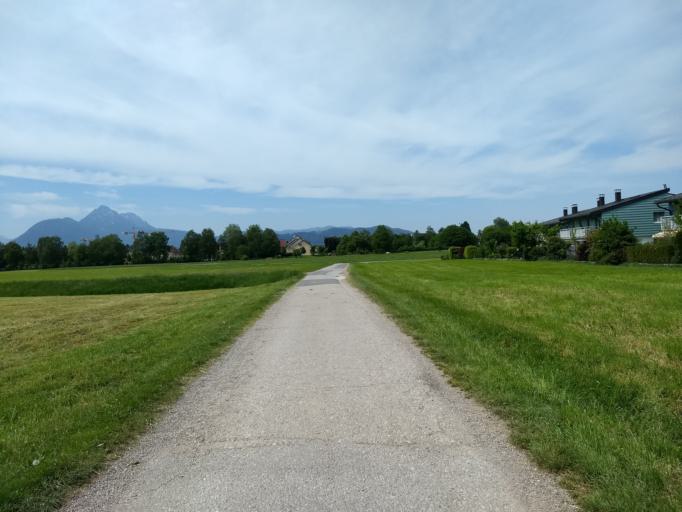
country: AT
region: Salzburg
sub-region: Salzburg Stadt
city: Salzburg
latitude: 47.7889
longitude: 13.0256
